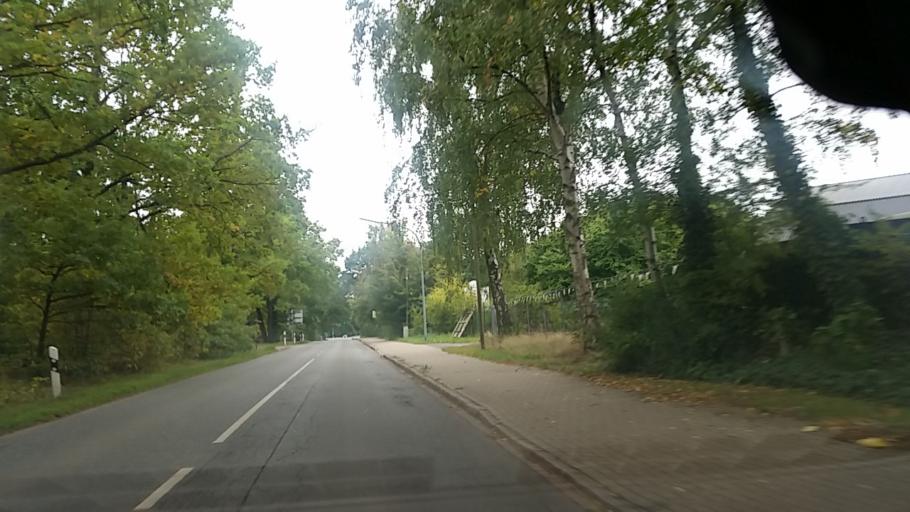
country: DE
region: Hamburg
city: Hummelsbuettel
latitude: 53.6834
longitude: 10.0461
